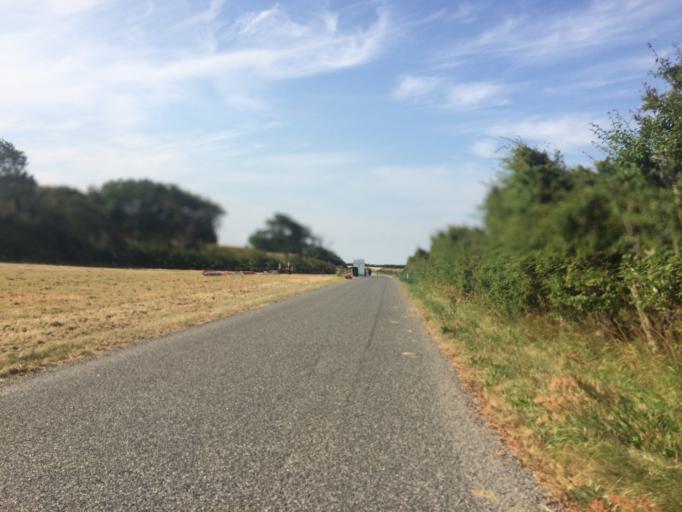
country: DK
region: Central Jutland
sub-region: Holstebro Kommune
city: Vinderup
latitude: 56.6417
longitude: 8.7821
